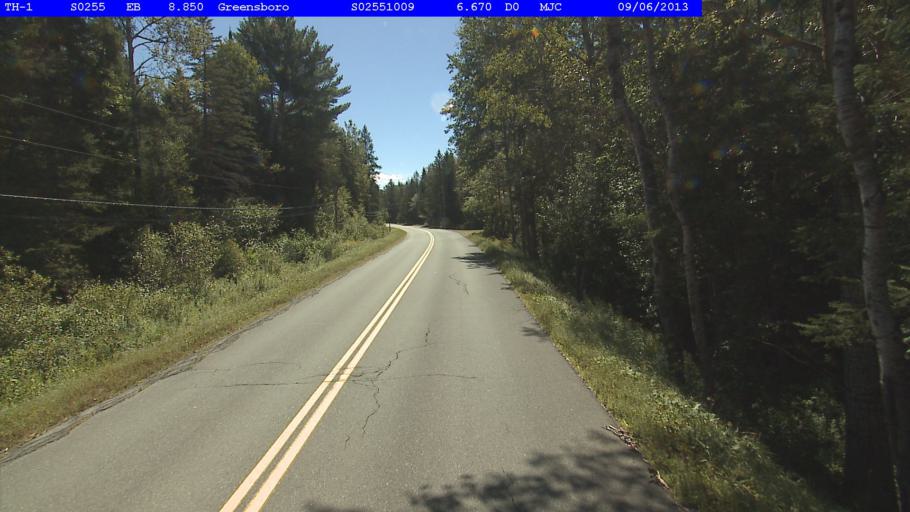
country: US
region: Vermont
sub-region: Caledonia County
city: Hardwick
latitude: 44.5582
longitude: -72.2772
